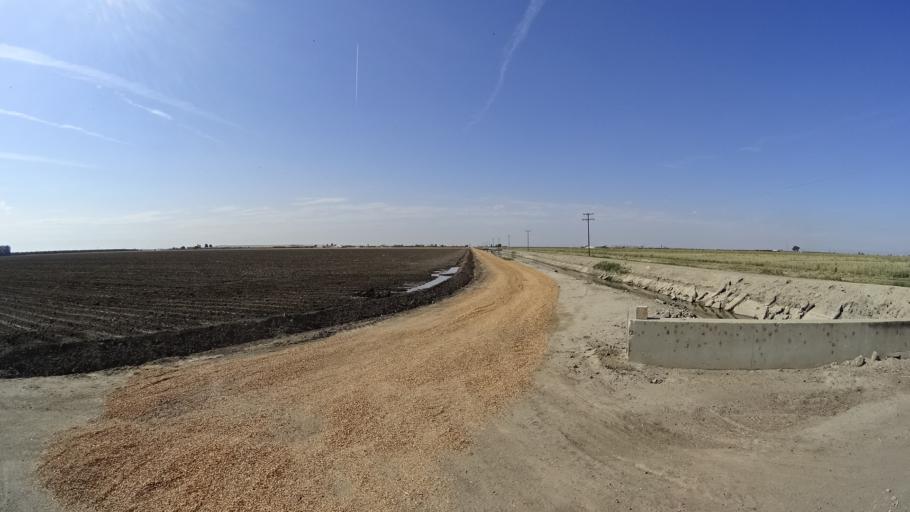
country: US
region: California
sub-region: Kings County
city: Home Garden
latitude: 36.2261
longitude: -119.5383
